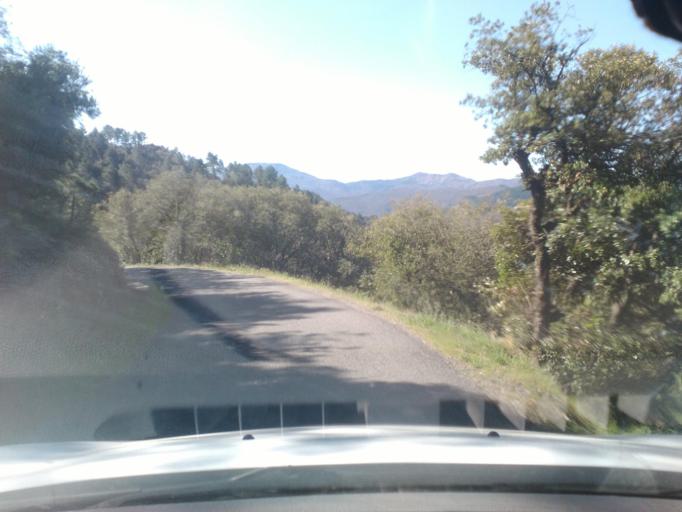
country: FR
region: Languedoc-Roussillon
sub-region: Departement du Gard
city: Saint-Jean-du-Gard
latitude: 44.1451
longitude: 3.7732
